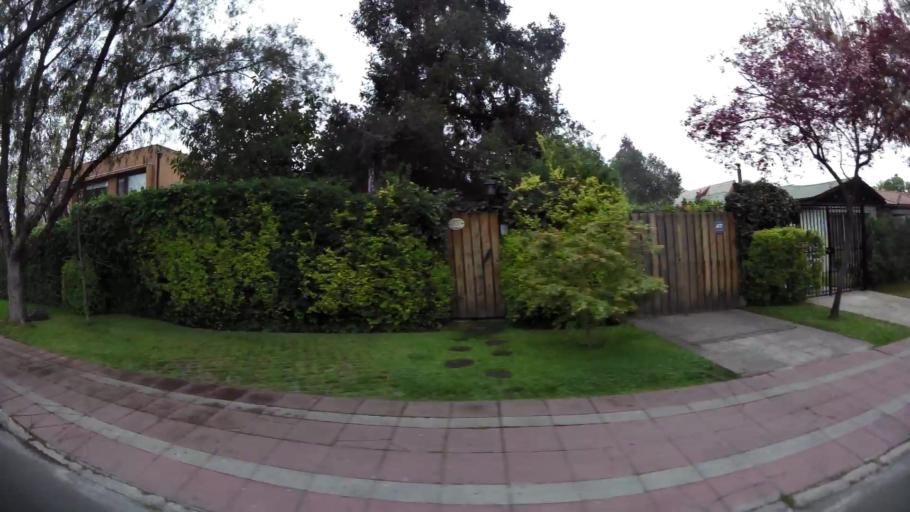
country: CL
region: Santiago Metropolitan
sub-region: Provincia de Santiago
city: Villa Presidente Frei, Nunoa, Santiago, Chile
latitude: -33.3926
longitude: -70.5660
